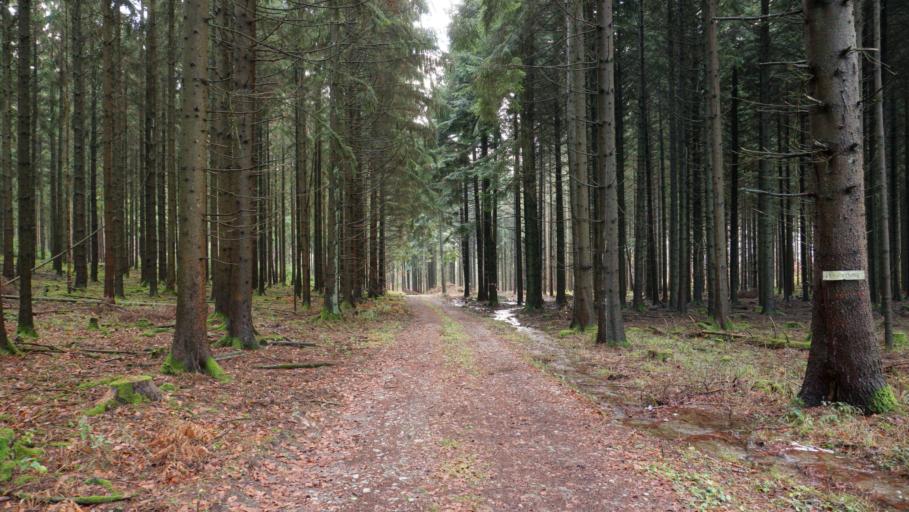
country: DE
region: Baden-Wuerttemberg
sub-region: Karlsruhe Region
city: Fahrenbach
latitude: 49.4328
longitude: 9.1129
